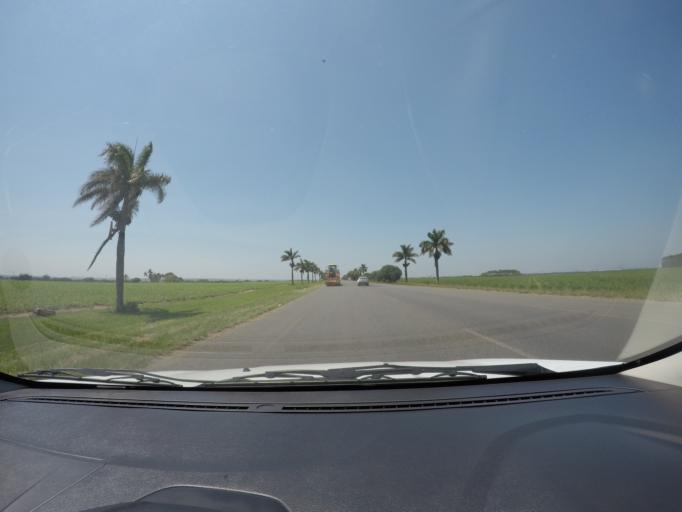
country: ZA
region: KwaZulu-Natal
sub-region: uThungulu District Municipality
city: eSikhawini
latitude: -28.8139
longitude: 31.9548
